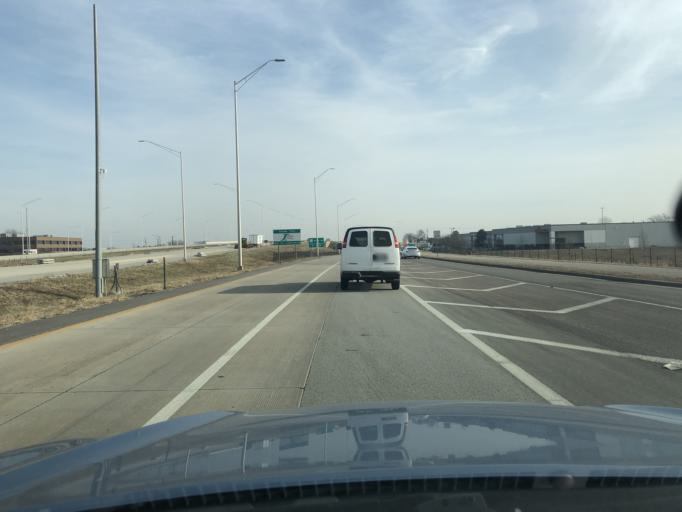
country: US
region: Illinois
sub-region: Cook County
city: Elk Grove Village
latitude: 41.9828
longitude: -87.9643
